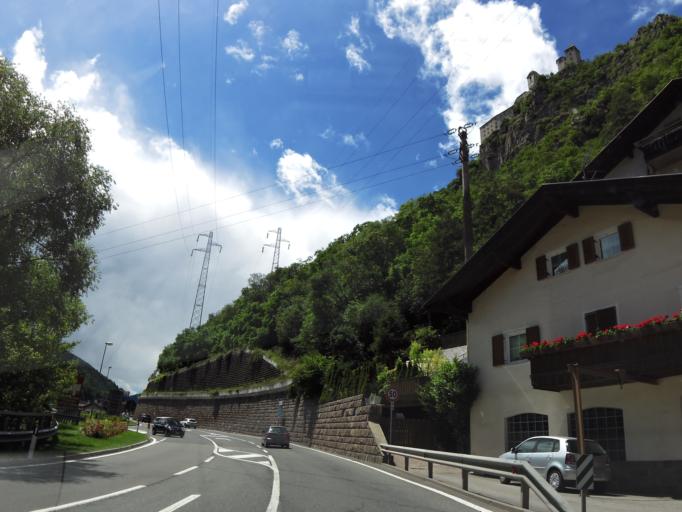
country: IT
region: Trentino-Alto Adige
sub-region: Bolzano
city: Chiusa
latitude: 46.6449
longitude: 11.5717
